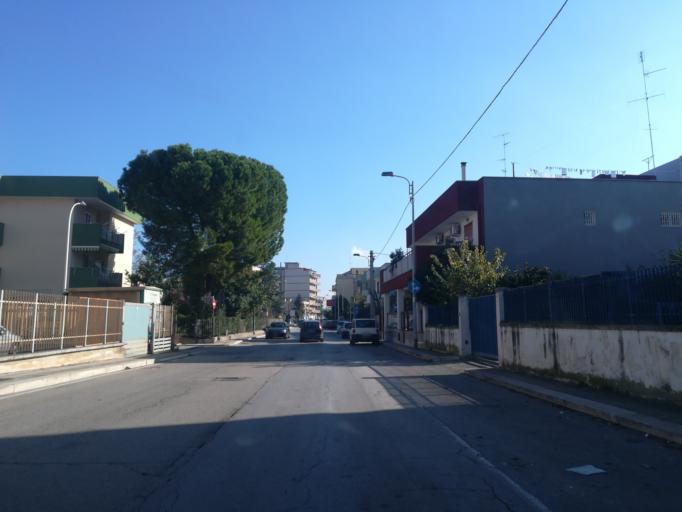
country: IT
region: Apulia
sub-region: Provincia di Bari
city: Modugno
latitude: 41.0770
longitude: 16.7823
